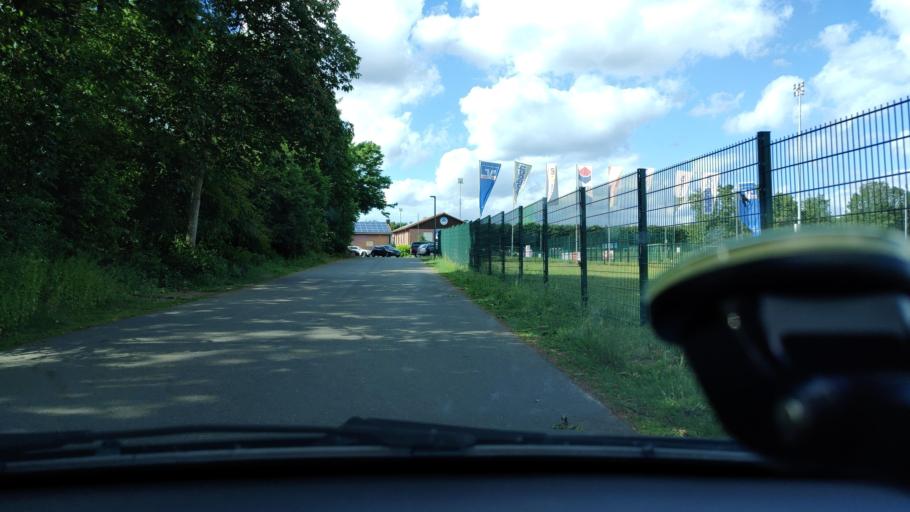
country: DE
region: North Rhine-Westphalia
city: Stadtlohn
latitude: 51.9989
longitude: 6.9291
